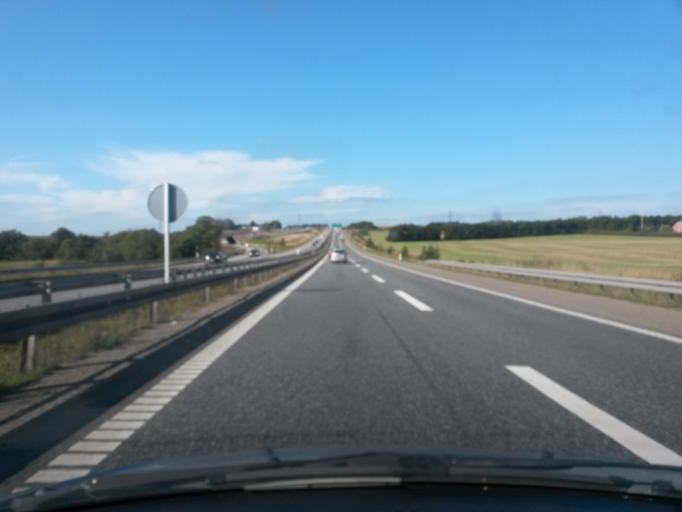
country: DK
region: Central Jutland
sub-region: Arhus Kommune
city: Trige
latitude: 56.2205
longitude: 10.1305
